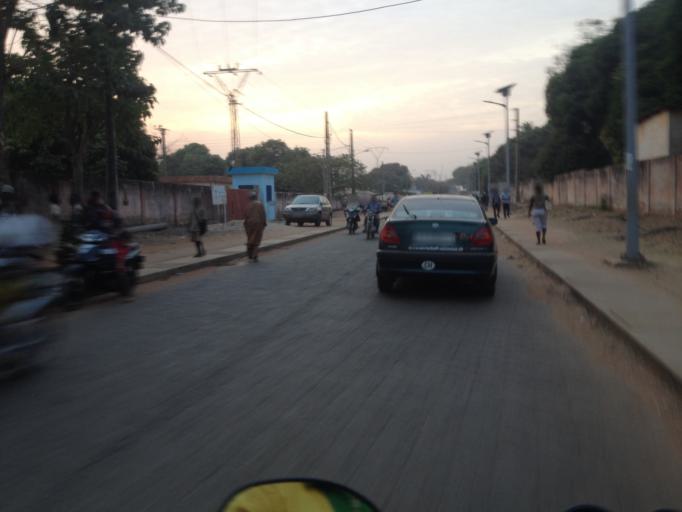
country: BJ
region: Borgou
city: Parakou
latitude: 9.3363
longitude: 2.6406
